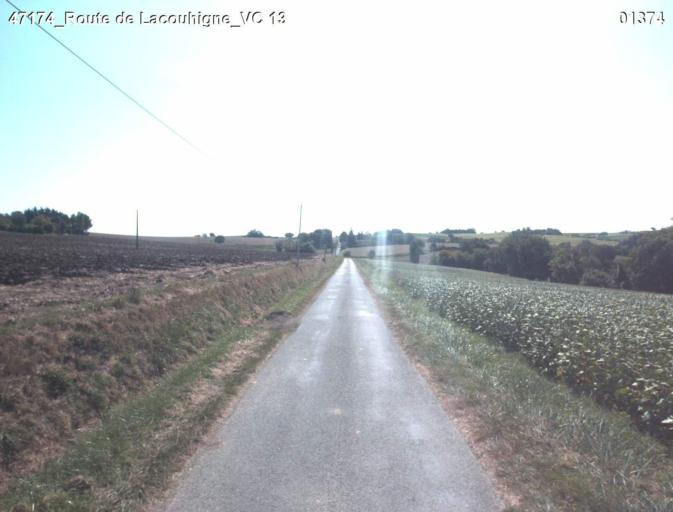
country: FR
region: Midi-Pyrenees
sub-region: Departement du Gers
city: Condom
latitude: 44.0243
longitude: 0.3779
